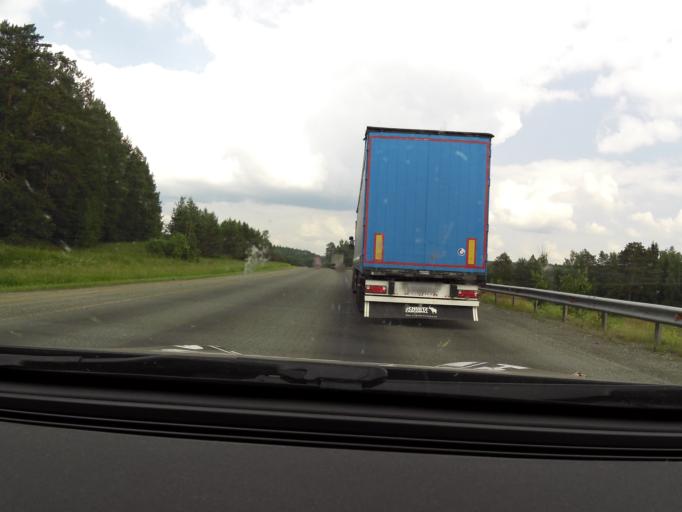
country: RU
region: Sverdlovsk
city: Ufimskiy
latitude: 56.7780
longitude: 58.2566
